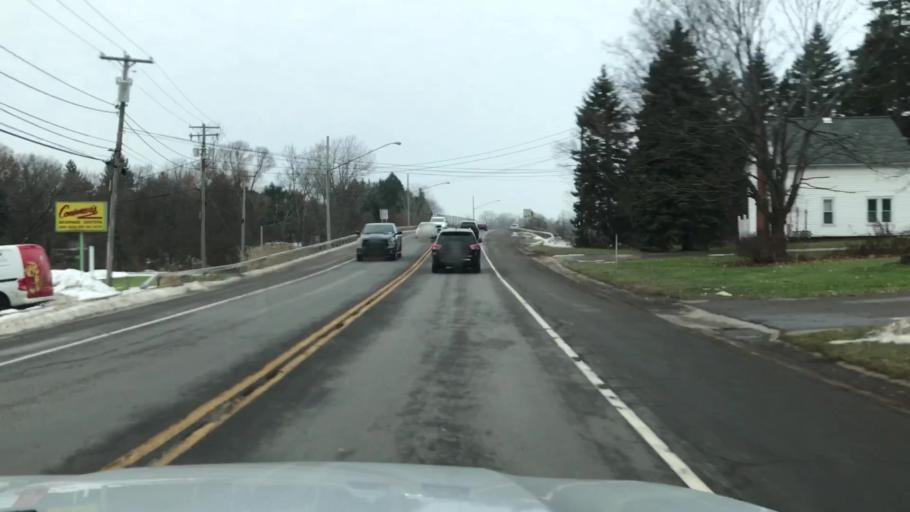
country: US
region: New York
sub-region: Erie County
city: Orchard Park
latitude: 42.7641
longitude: -78.7548
